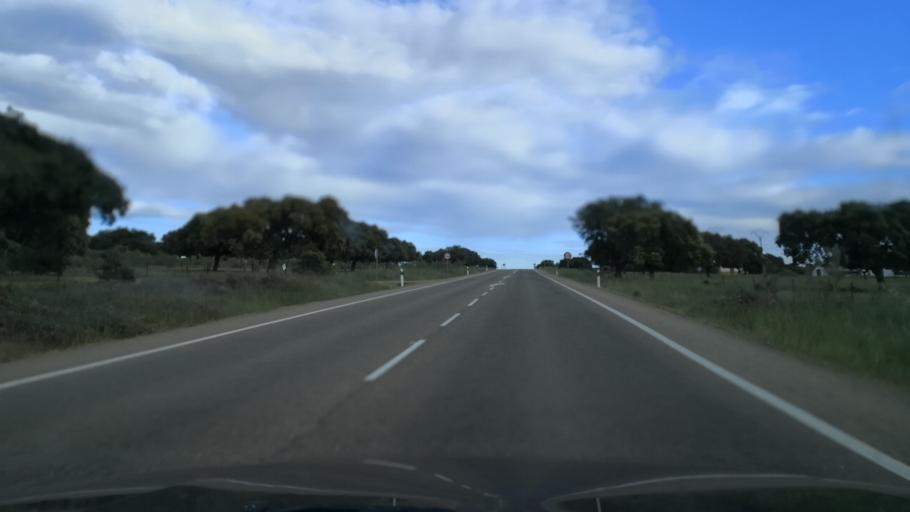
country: ES
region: Extremadura
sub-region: Provincia de Caceres
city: Torrejoncillo
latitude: 39.9241
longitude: -6.4975
